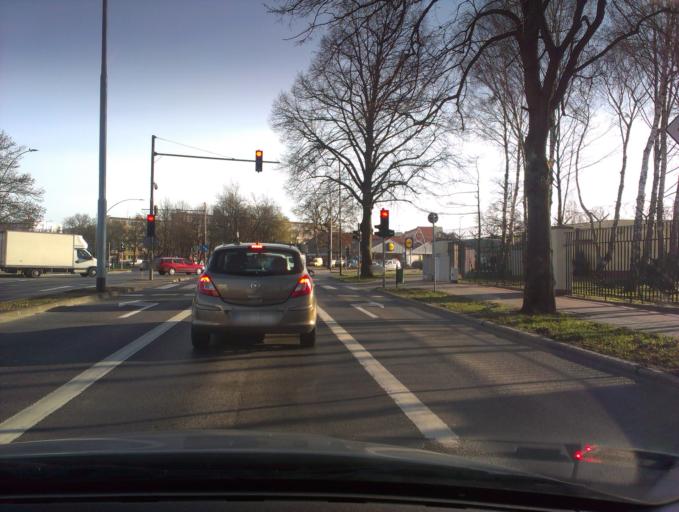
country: PL
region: West Pomeranian Voivodeship
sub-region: Koszalin
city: Koszalin
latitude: 54.1905
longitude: 16.2107
